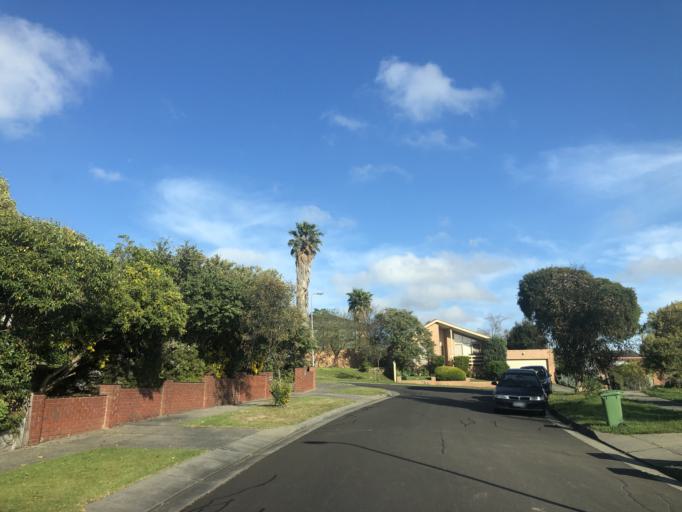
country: AU
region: Victoria
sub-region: Casey
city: Eumemmerring
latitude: -37.9981
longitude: 145.2596
